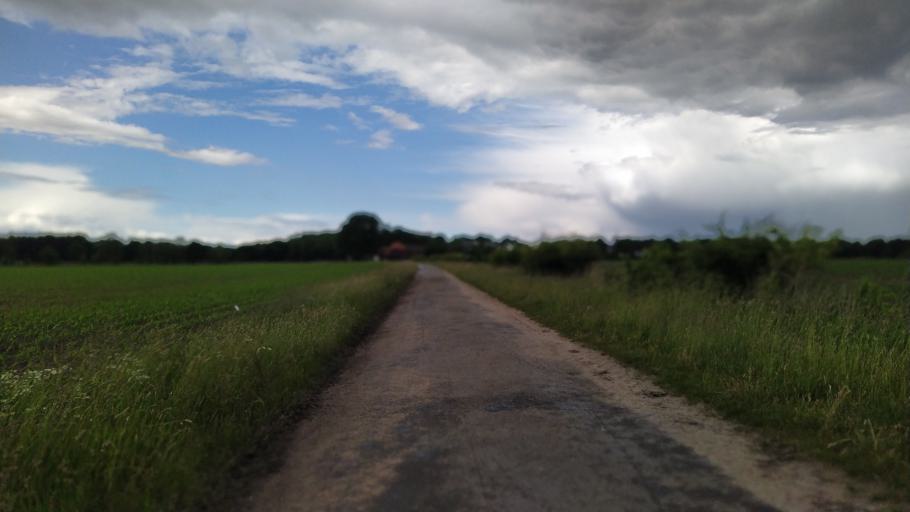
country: DE
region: Lower Saxony
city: Kutenholz
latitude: 53.4635
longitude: 9.3453
